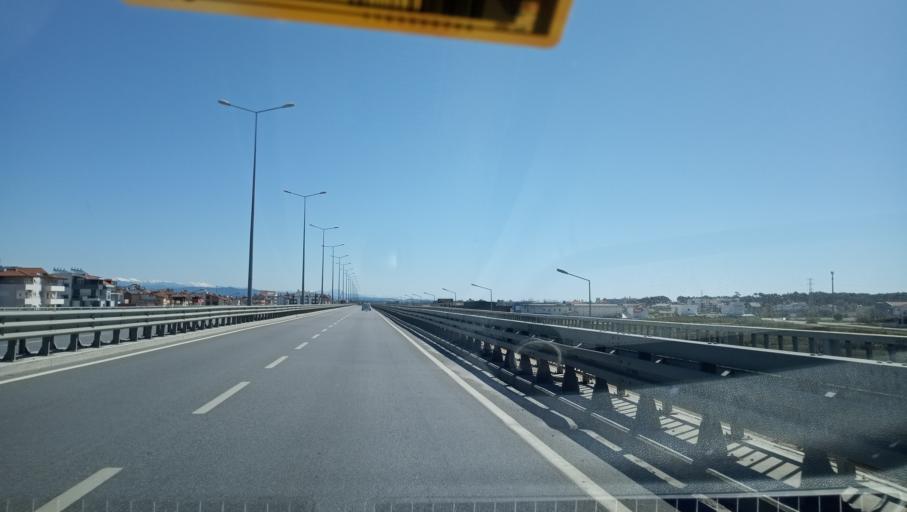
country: TR
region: Antalya
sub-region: Manavgat
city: Manavgat
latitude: 36.7800
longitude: 31.4306
